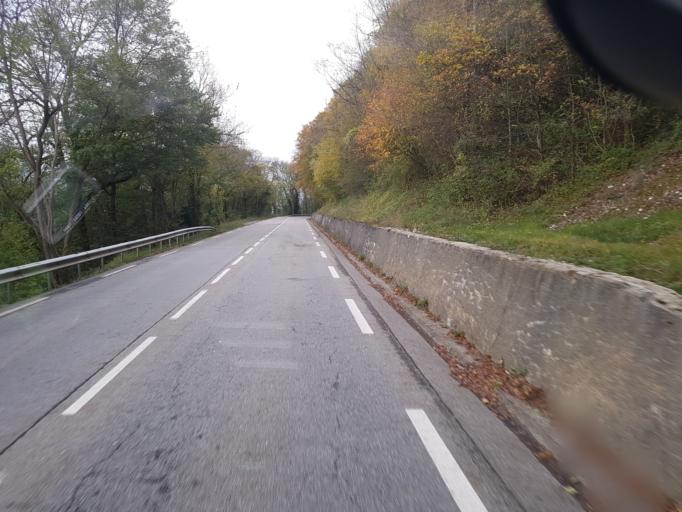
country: FR
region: Rhone-Alpes
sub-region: Departement de l'Isere
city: Le Gua
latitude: 44.9676
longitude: 5.6380
